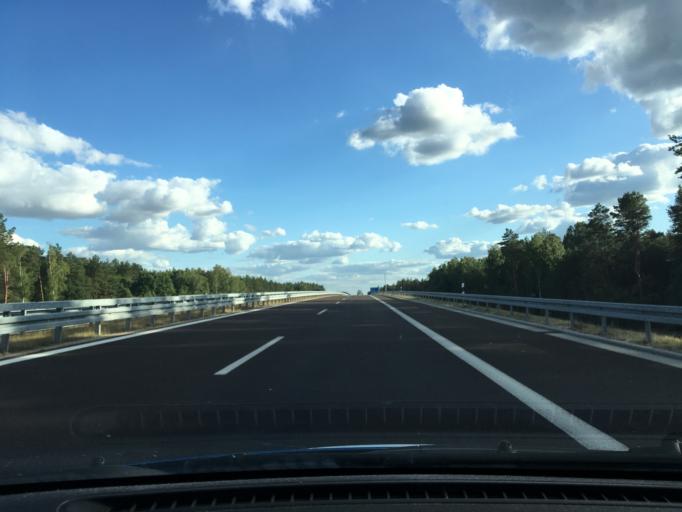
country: DE
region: Mecklenburg-Vorpommern
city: Ludwigslust
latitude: 53.3091
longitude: 11.5275
